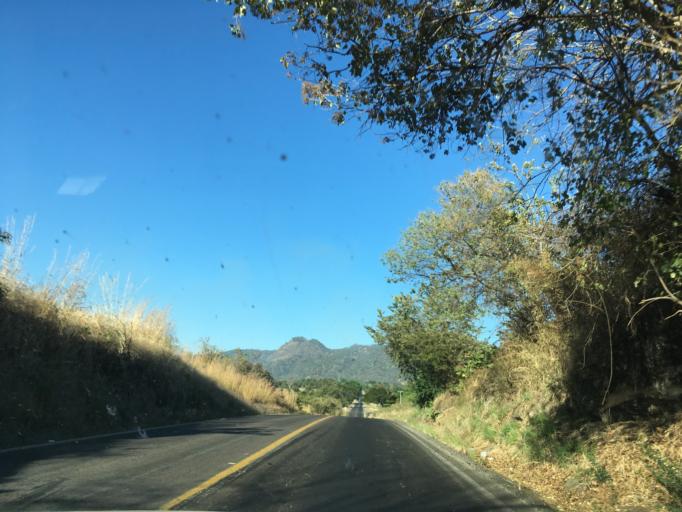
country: MX
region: Michoacan
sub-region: Gabriel Zamora
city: Lombardia
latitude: 19.2002
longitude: -102.0541
